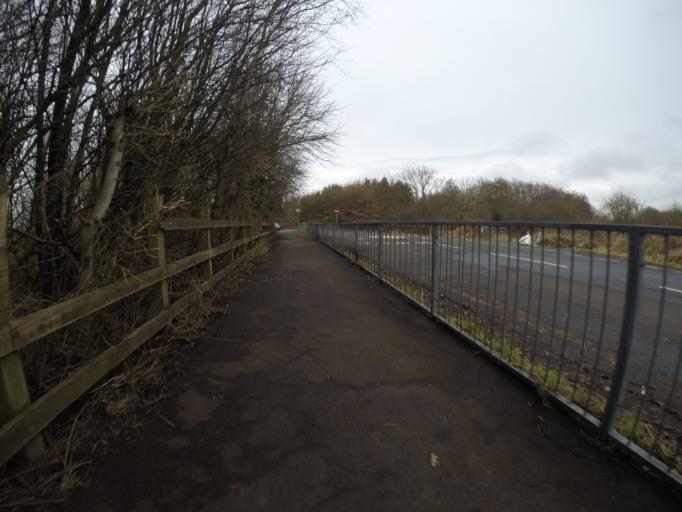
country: GB
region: Scotland
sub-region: North Ayrshire
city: Kilwinning
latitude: 55.6397
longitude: -4.6909
